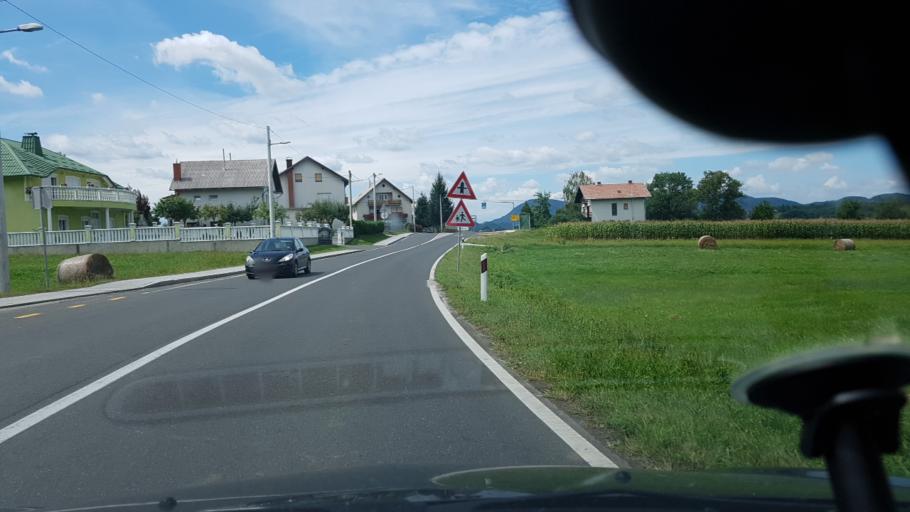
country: HR
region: Varazdinska
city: Ivanec
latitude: 46.2232
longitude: 16.0937
